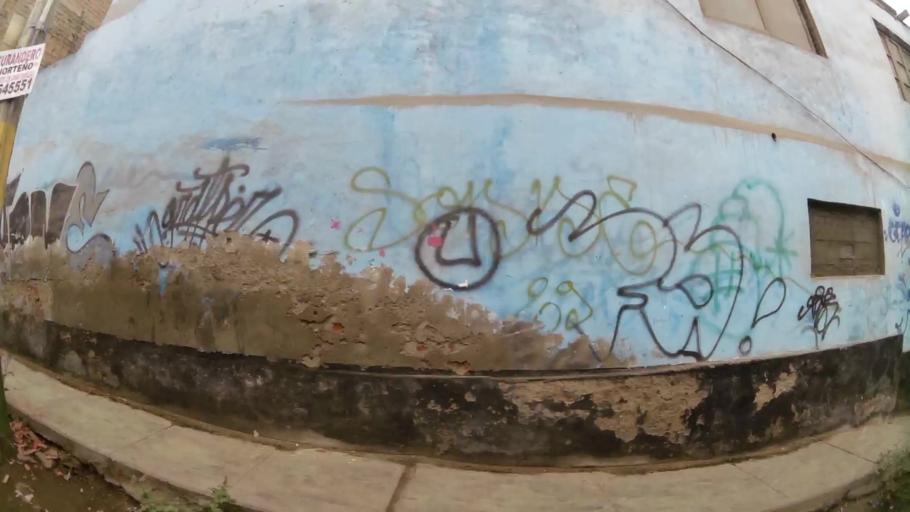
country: PE
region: Lima
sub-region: Lima
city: Surco
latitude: -12.1750
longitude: -76.9365
